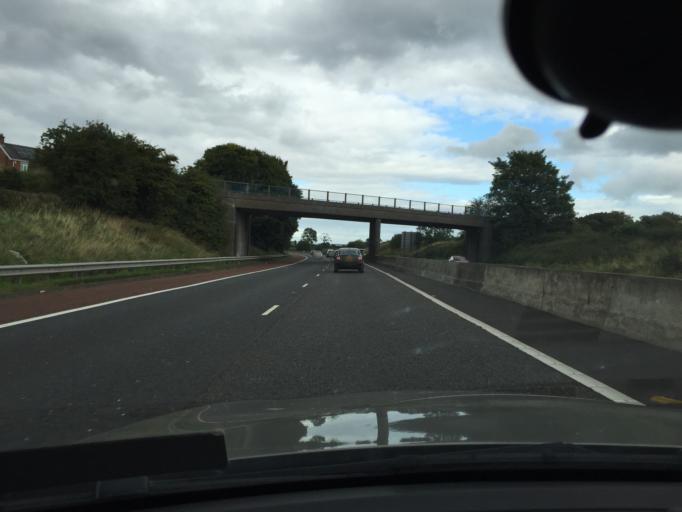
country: GB
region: Northern Ireland
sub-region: Lisburn District
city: Lisburn
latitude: 54.5124
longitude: -6.0161
